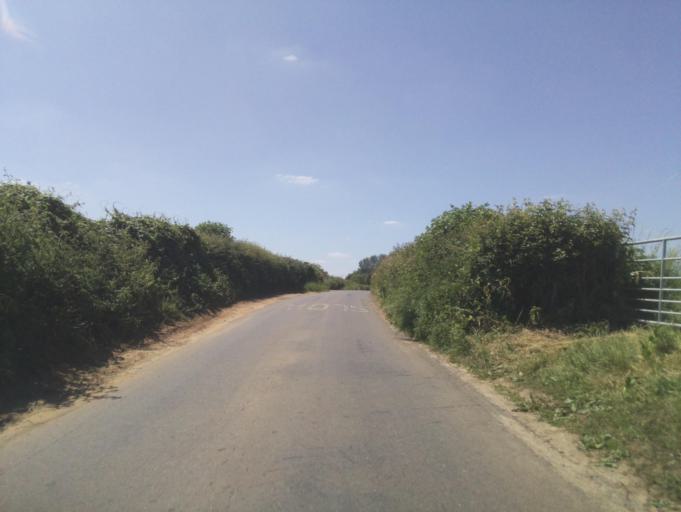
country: GB
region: England
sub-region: Wiltshire
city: Bremhill
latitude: 51.4552
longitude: -2.0381
